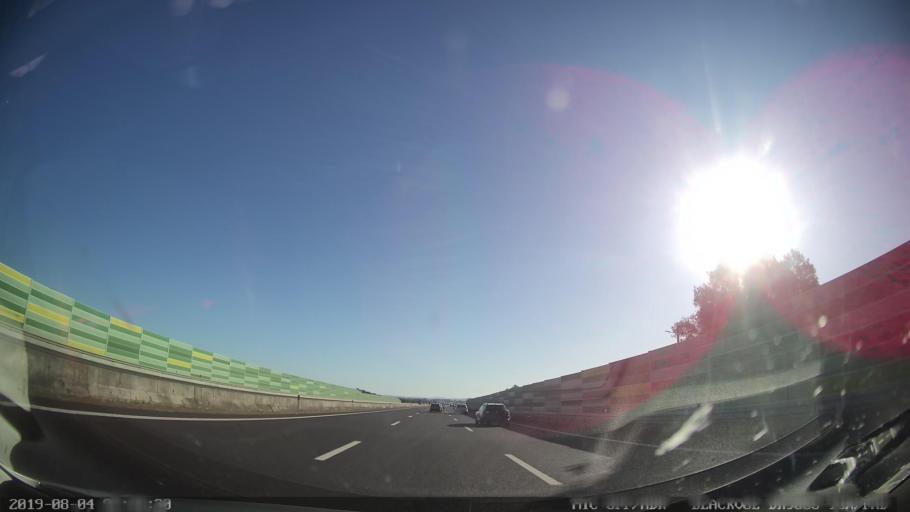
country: PT
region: Santarem
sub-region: Cartaxo
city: Pontevel
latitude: 39.1770
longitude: -8.8358
